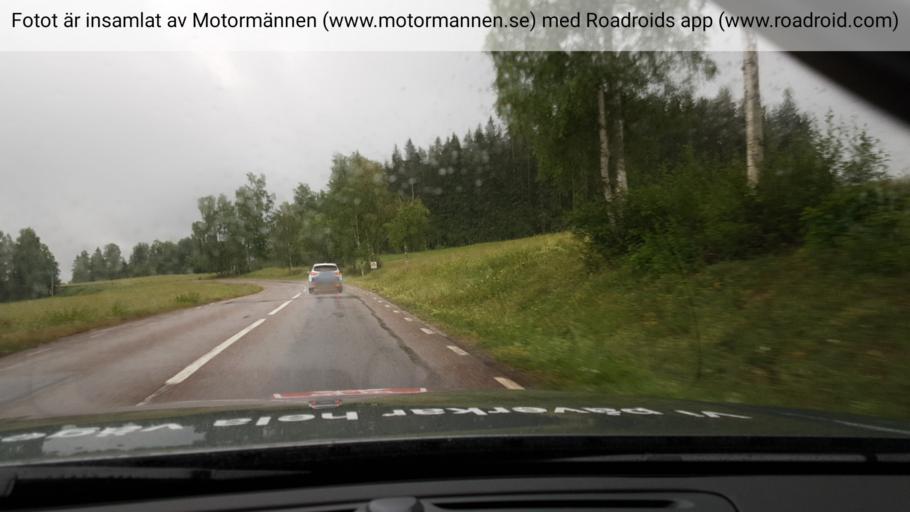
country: SE
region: Dalarna
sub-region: Avesta Kommun
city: Avesta
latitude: 59.9936
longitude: 16.1040
